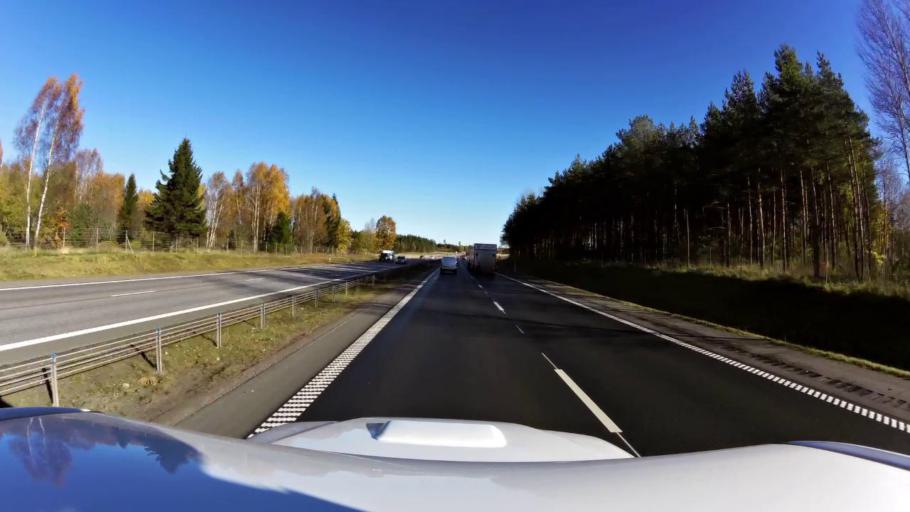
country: SE
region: OEstergoetland
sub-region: Linkopings Kommun
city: Vikingstad
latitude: 58.4000
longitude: 15.4342
